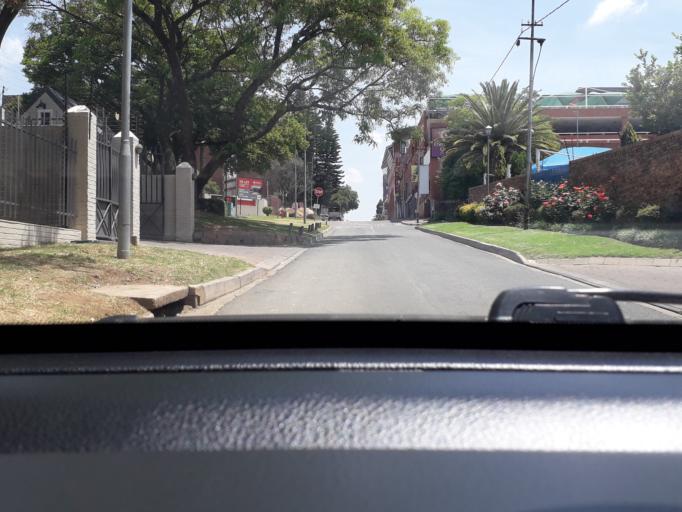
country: ZA
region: Gauteng
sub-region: City of Johannesburg Metropolitan Municipality
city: Midrand
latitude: -26.0574
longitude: 28.0624
